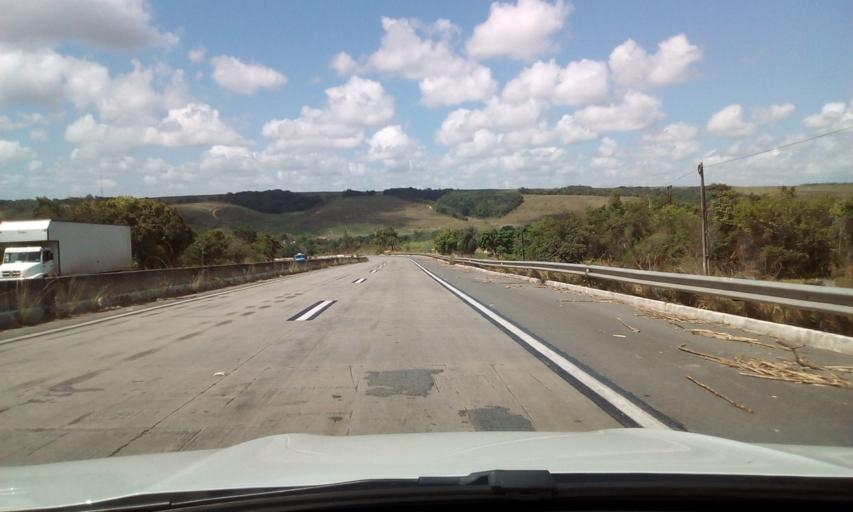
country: BR
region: Paraiba
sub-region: Alhandra
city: Alhandra
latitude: -7.4709
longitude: -34.9771
